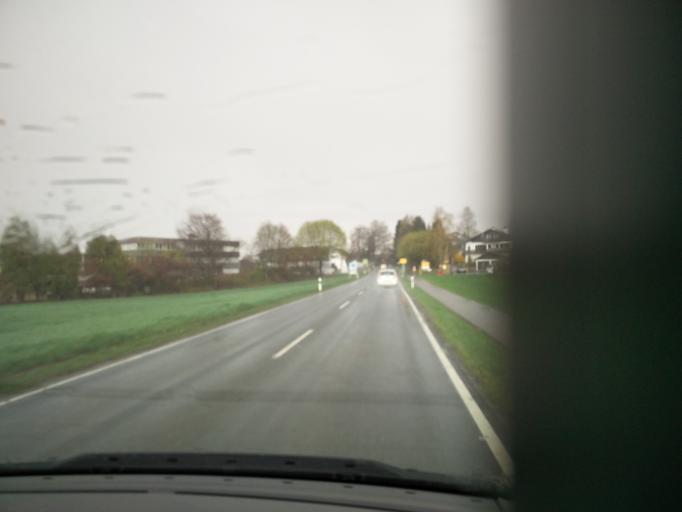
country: DE
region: Bavaria
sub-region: Upper Bavaria
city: Rimsting
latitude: 47.8853
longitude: 12.3330
